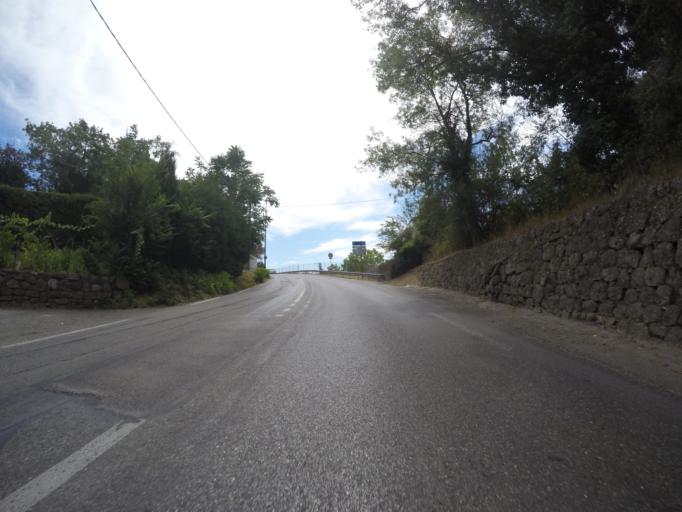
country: FR
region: Provence-Alpes-Cote d'Azur
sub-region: Departement des Alpes-Maritimes
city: Mougins
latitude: 43.6059
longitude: 6.9988
